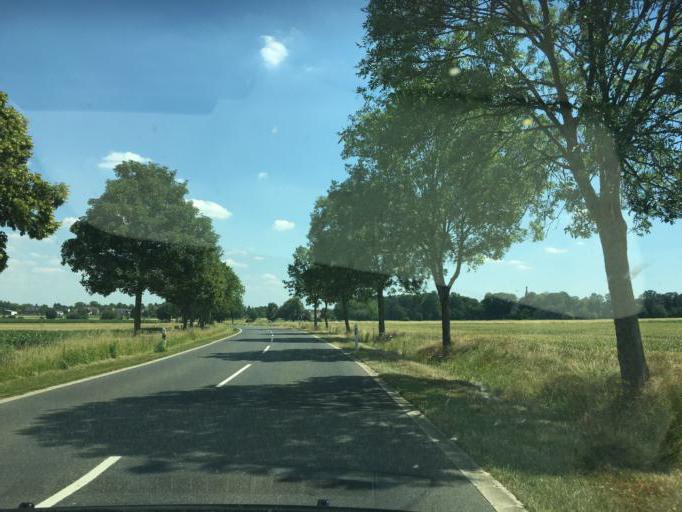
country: DE
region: North Rhine-Westphalia
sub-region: Regierungsbezirk Koln
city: Langerwehe
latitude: 50.8058
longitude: 6.3830
